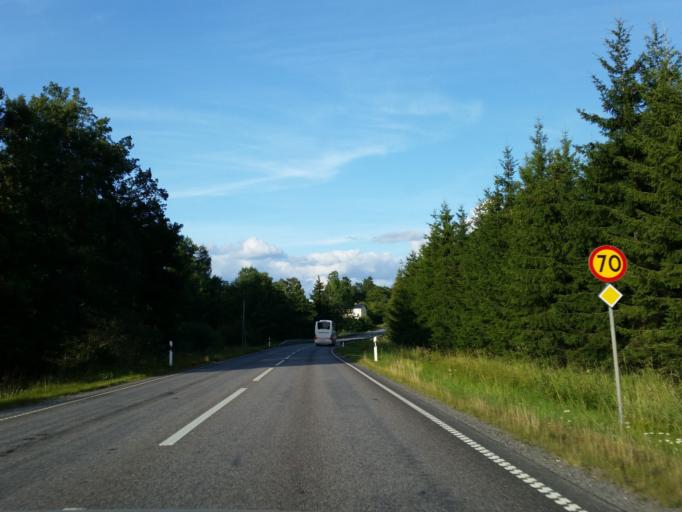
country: SE
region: Stockholm
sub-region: Sodertalje Kommun
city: Molnbo
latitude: 59.0426
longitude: 17.3998
